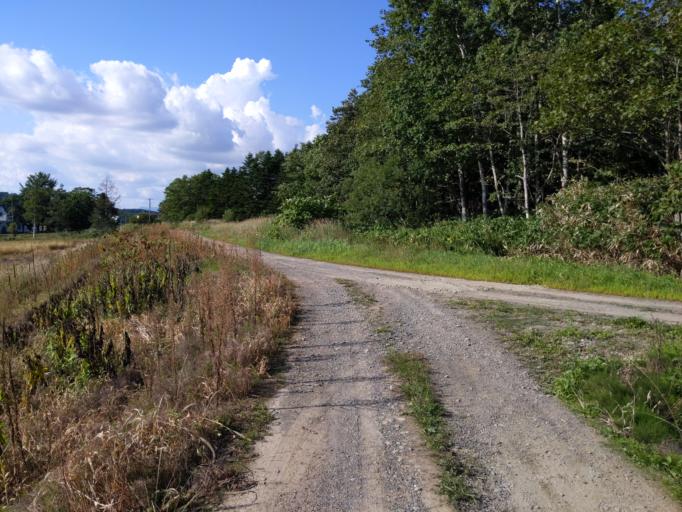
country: JP
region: Hokkaido
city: Iwamizawa
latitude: 43.1941
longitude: 141.8300
